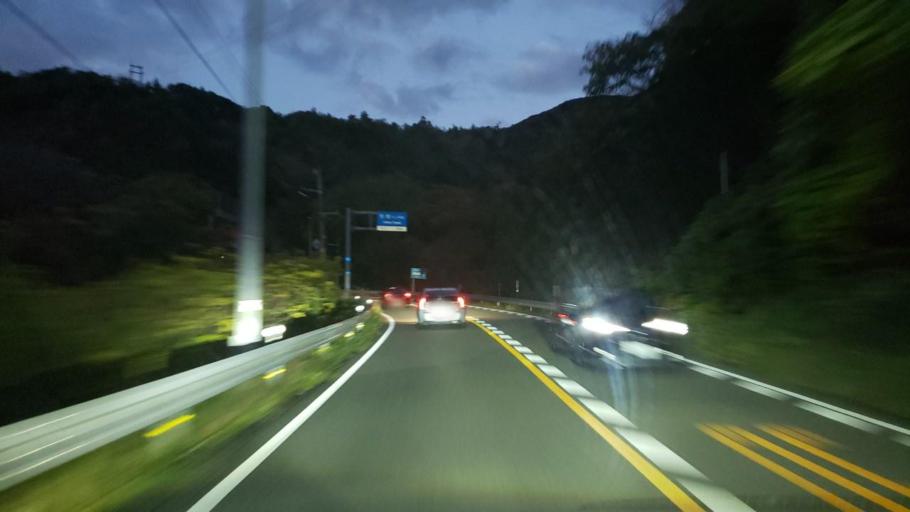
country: JP
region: Tokushima
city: Ishii
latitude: 34.2067
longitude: 134.4371
